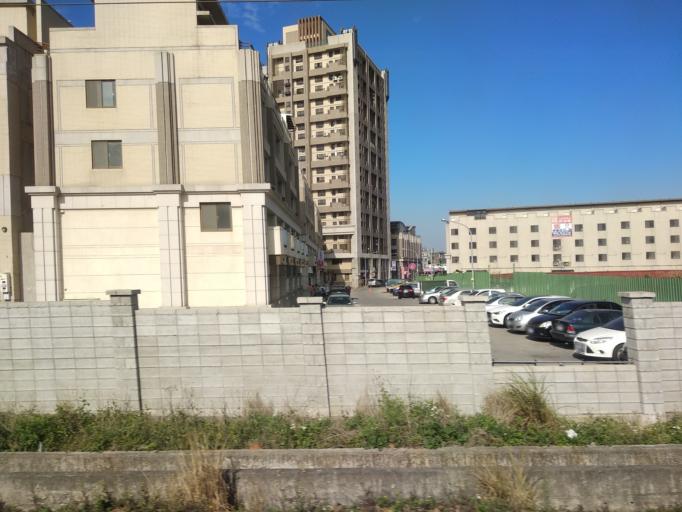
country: TW
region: Taiwan
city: Taoyuan City
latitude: 24.9668
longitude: 121.2489
